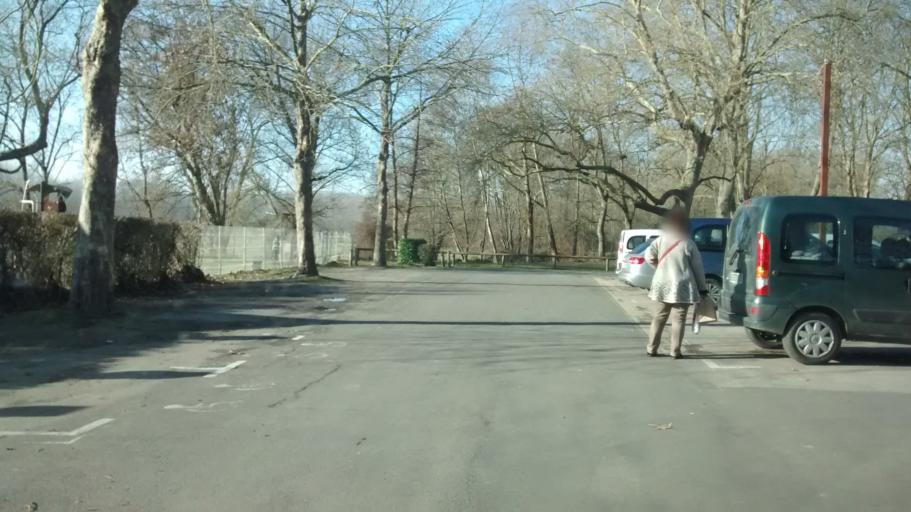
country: FR
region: Centre
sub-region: Departement d'Indre-et-Loire
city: Azay-le-Rideau
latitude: 47.2597
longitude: 0.4643
